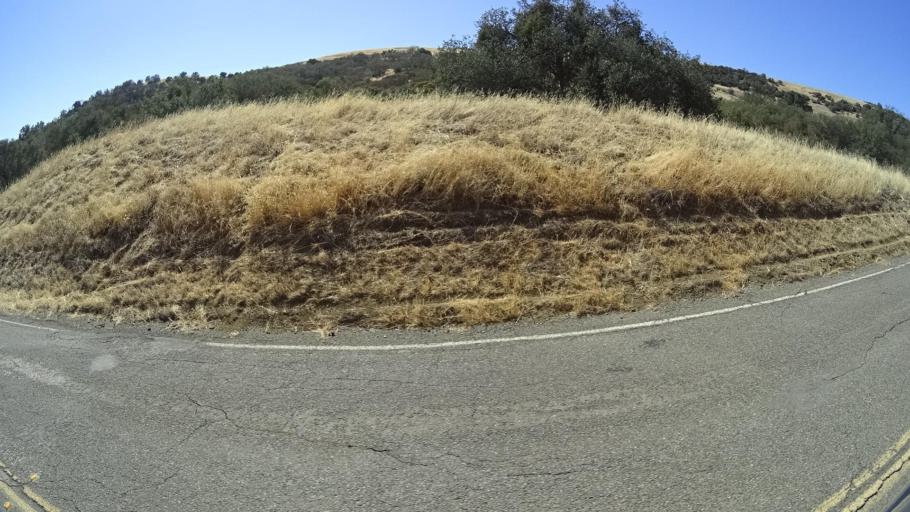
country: US
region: California
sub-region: San Luis Obispo County
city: Lake Nacimiento
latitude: 35.8452
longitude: -121.0465
